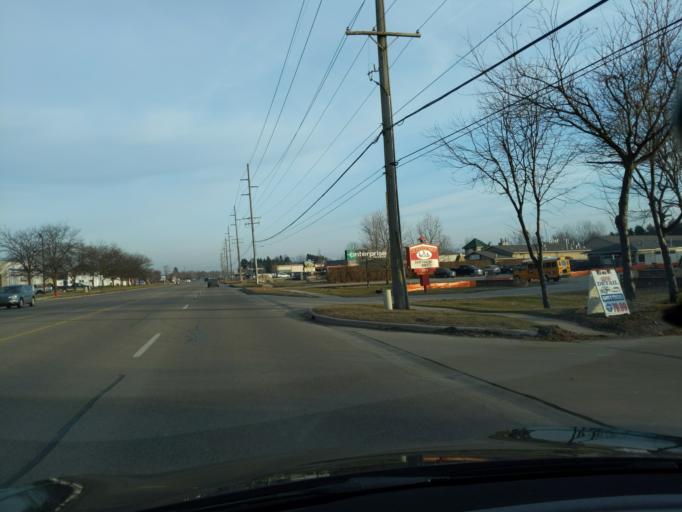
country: US
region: Michigan
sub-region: Livingston County
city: Brighton
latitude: 42.5686
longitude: -83.8133
